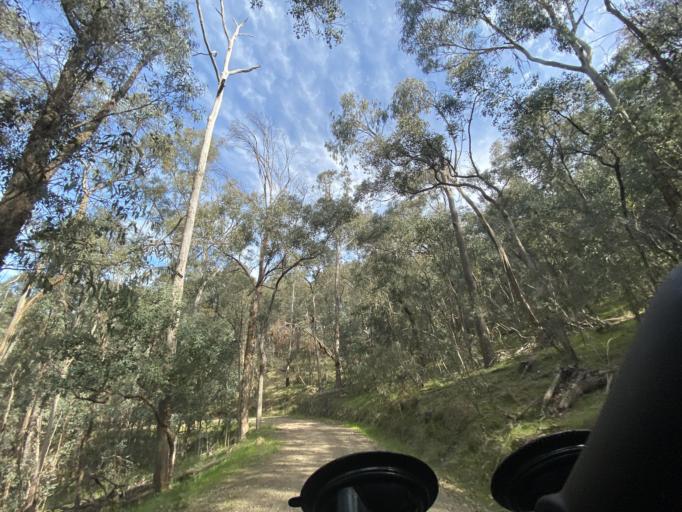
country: AU
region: Victoria
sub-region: Mansfield
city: Mansfield
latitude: -36.7984
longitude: 146.1140
